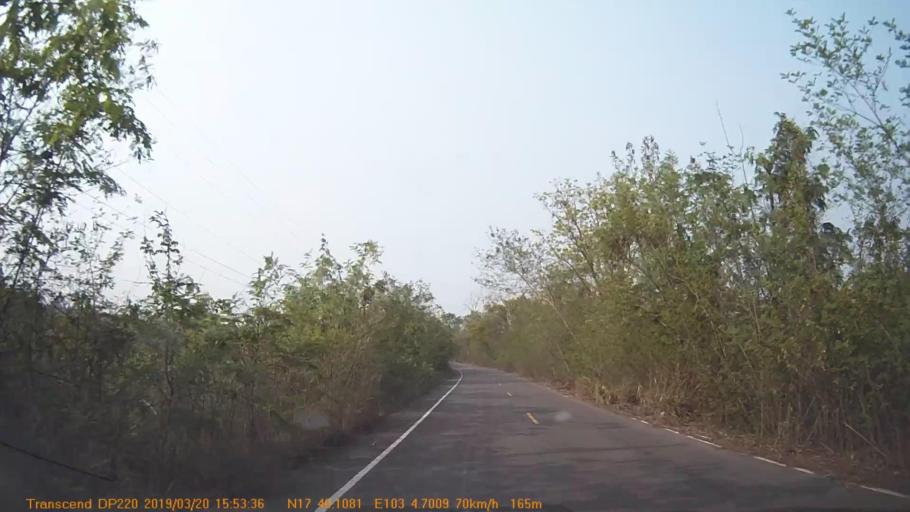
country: TH
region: Changwat Udon Thani
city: Phibun Rak
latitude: 17.6688
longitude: 103.0784
